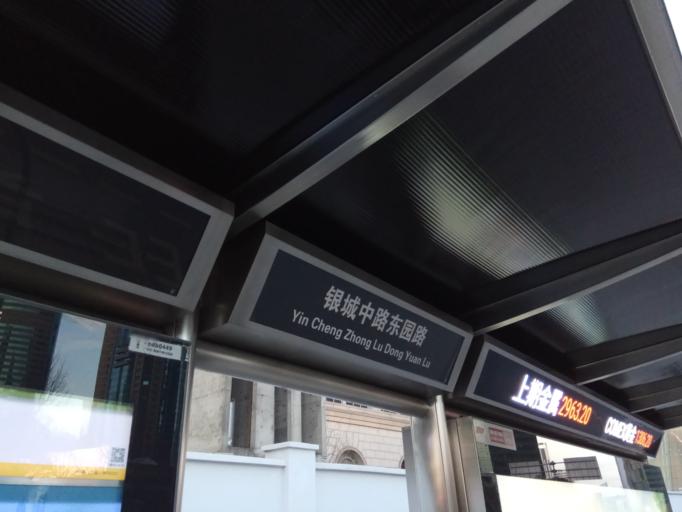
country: CN
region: Shanghai Shi
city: Hongkou
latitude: 31.2420
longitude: 121.5011
